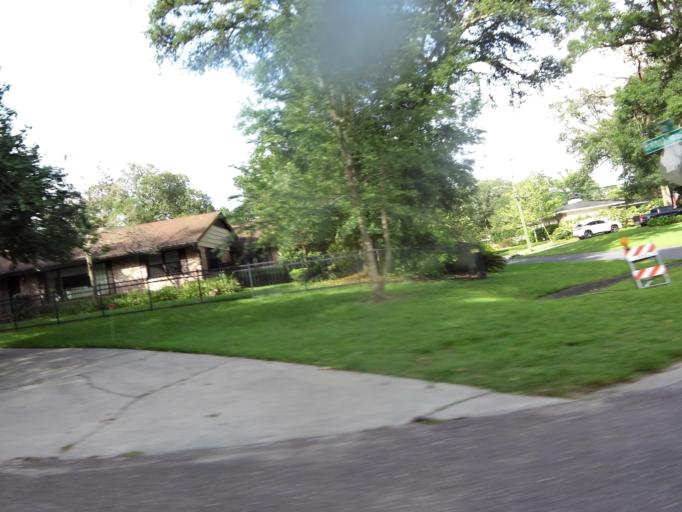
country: US
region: Florida
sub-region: Clay County
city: Bellair-Meadowbrook Terrace
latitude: 30.2610
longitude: -81.7116
